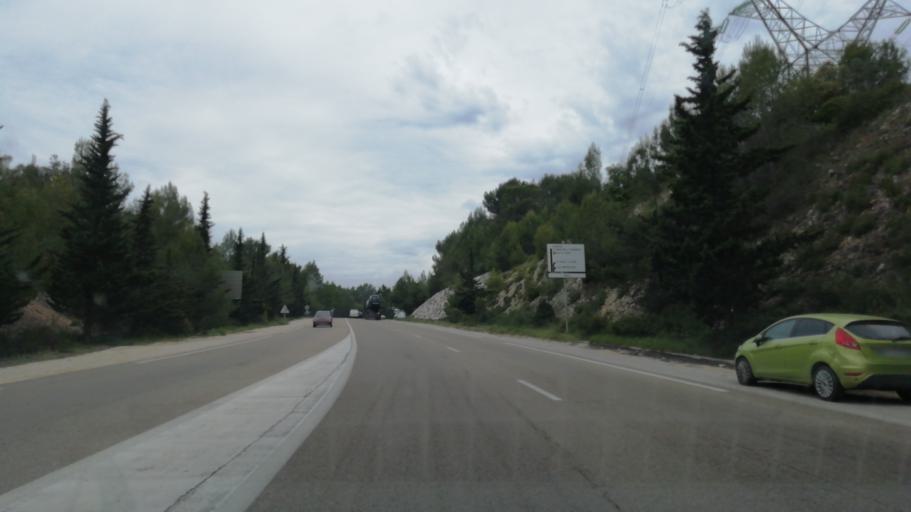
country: FR
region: Languedoc-Roussillon
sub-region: Departement de l'Herault
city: Saint-Gely-du-Fesc
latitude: 43.7083
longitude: 3.8167
